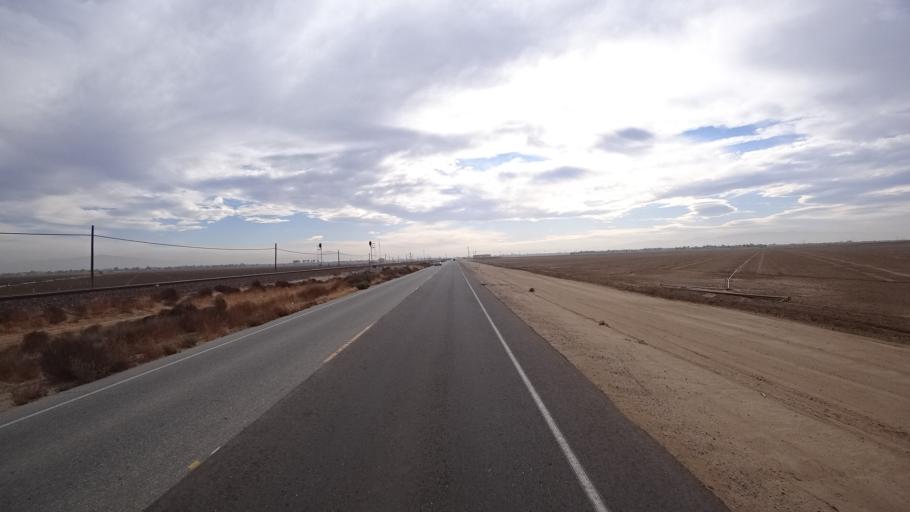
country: US
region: California
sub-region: Kern County
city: Rosedale
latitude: 35.4158
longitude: -119.1677
